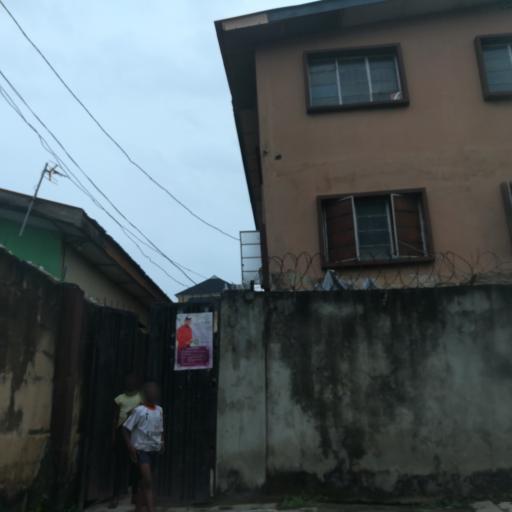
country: NG
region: Lagos
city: Ebute Metta
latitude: 6.4882
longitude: 3.3877
